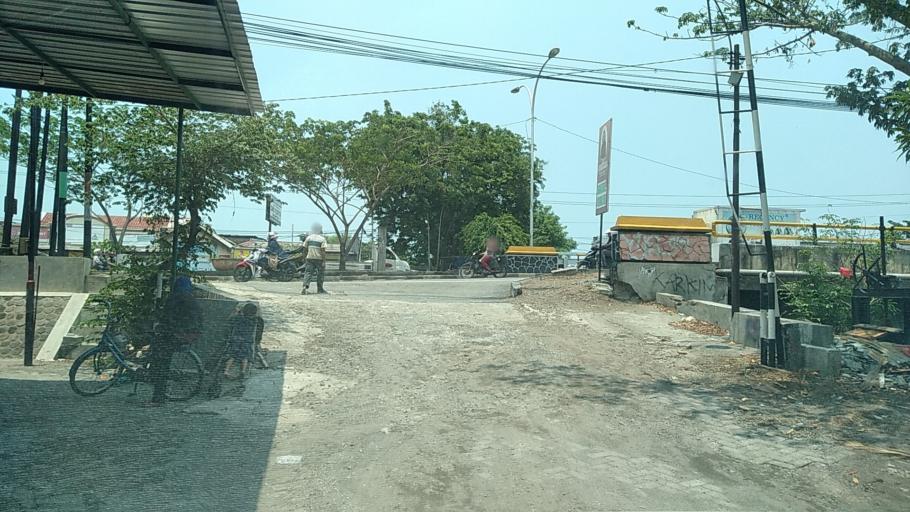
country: ID
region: Central Java
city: Semarang
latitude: -6.9607
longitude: 110.4409
